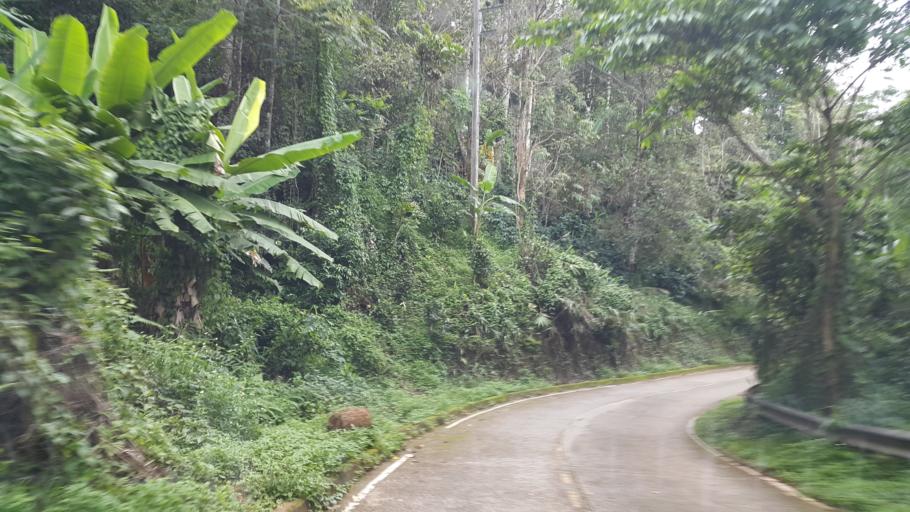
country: TH
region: Lampang
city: Mueang Pan
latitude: 18.8271
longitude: 99.3872
